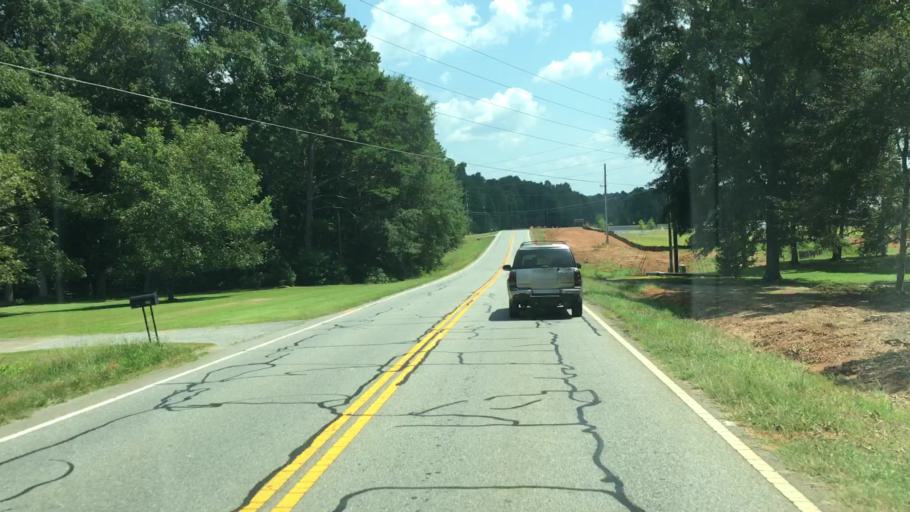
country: US
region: Georgia
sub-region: Barrow County
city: Statham
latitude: 33.9214
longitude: -83.6090
